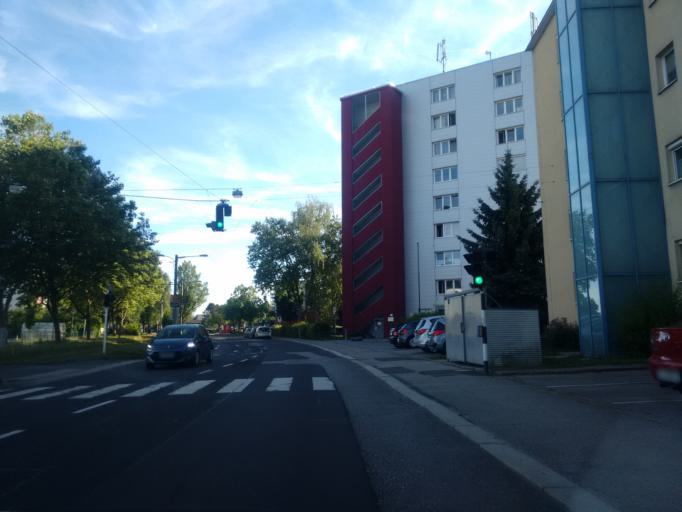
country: AT
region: Upper Austria
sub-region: Linz Stadt
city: Linz
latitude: 48.3339
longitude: 14.3187
